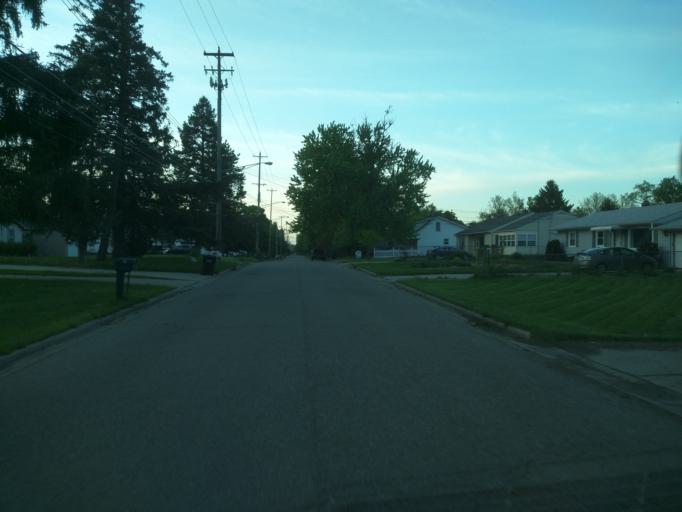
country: US
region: Michigan
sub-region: Eaton County
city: Waverly
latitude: 42.7346
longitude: -84.6091
